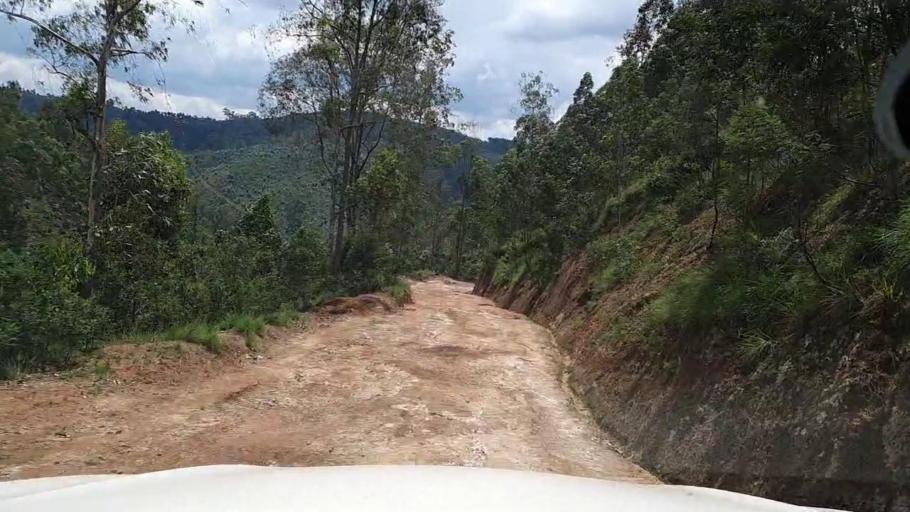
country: RW
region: Southern Province
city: Nzega
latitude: -2.6421
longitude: 29.4785
